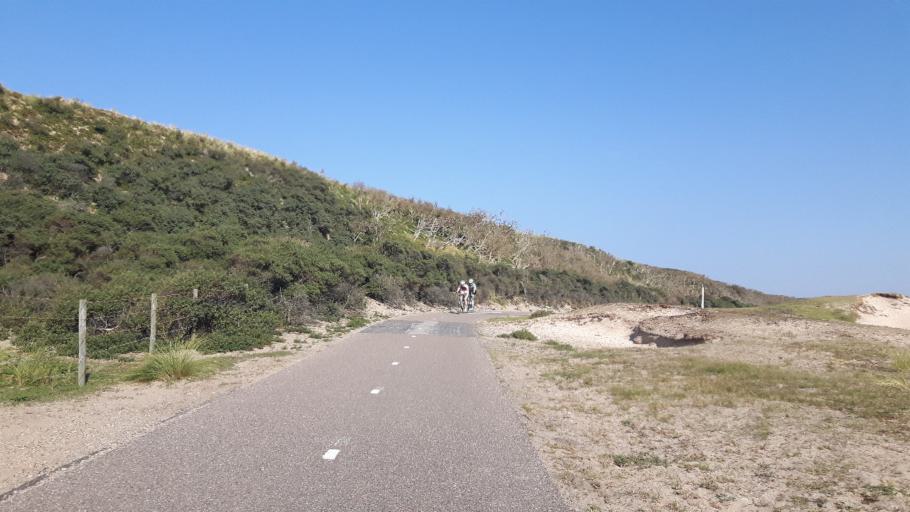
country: NL
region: North Holland
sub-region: Gemeente Zandvoort
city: Zandvoort
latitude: 52.3515
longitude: 4.5124
